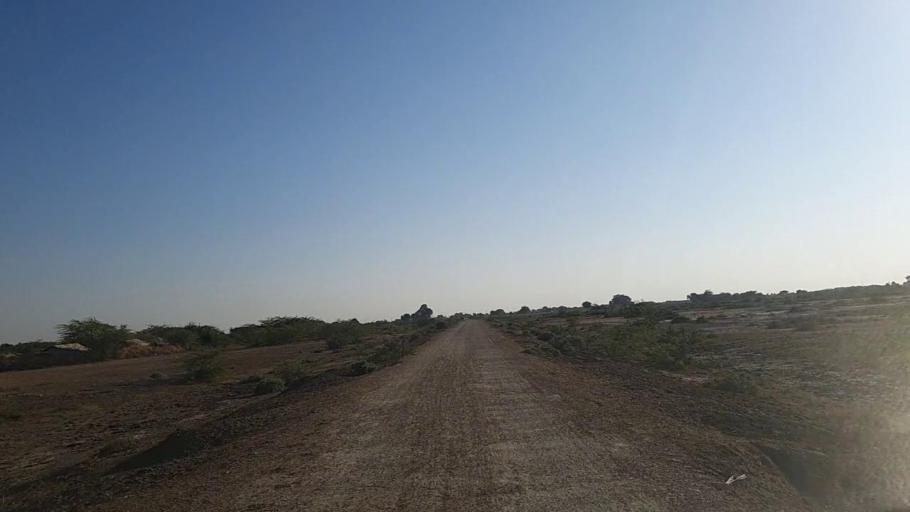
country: PK
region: Sindh
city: Naukot
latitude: 24.9551
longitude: 69.3884
